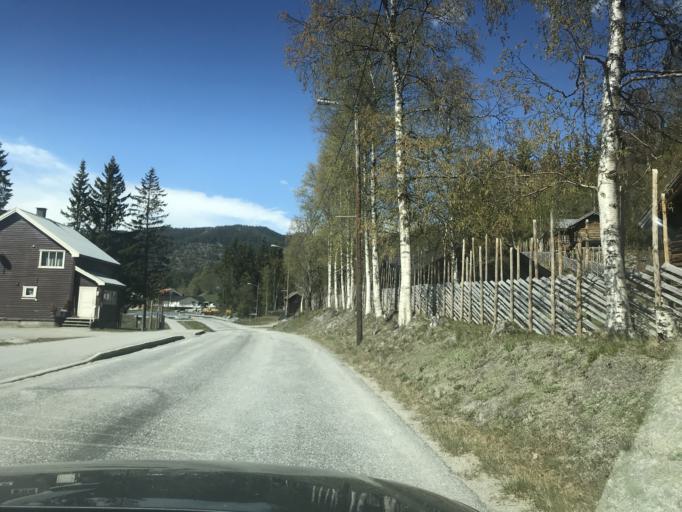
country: NO
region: Telemark
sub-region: Hjartdal
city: Sauland
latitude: 59.7539
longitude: 8.7960
